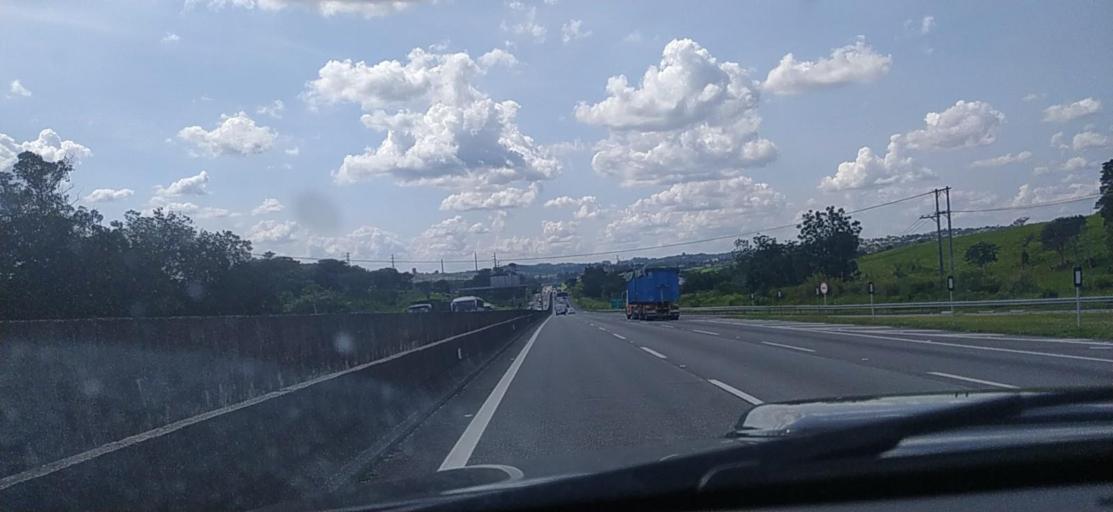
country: BR
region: Sao Paulo
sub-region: Louveira
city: Louveira
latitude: -23.0756
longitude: -46.9834
